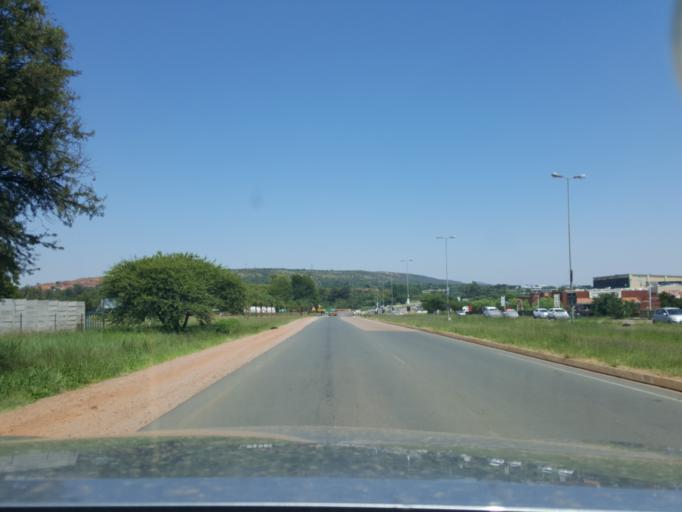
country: ZA
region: Gauteng
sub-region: City of Tshwane Metropolitan Municipality
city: Pretoria
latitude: -25.6848
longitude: 28.2972
